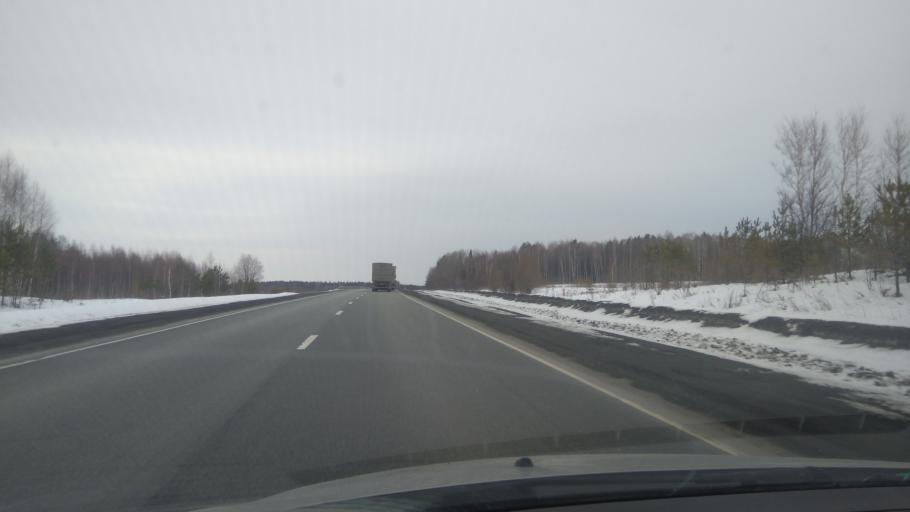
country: RU
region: Sverdlovsk
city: Bisert'
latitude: 56.8161
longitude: 58.7487
